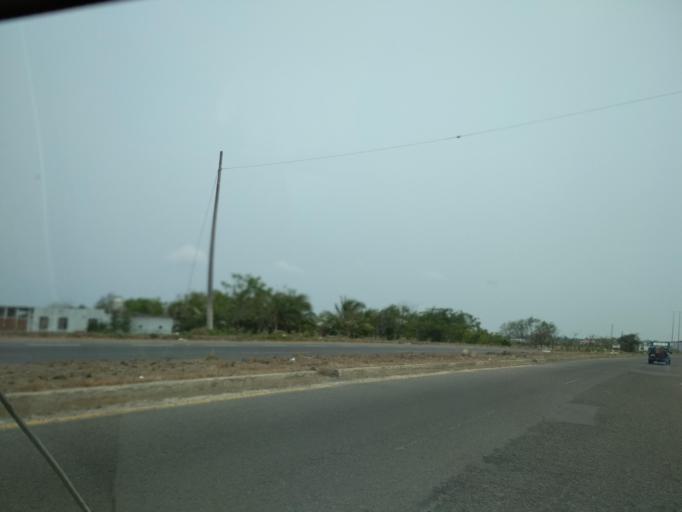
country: MX
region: Veracruz
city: Paso del Toro
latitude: 19.0475
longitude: -96.1333
